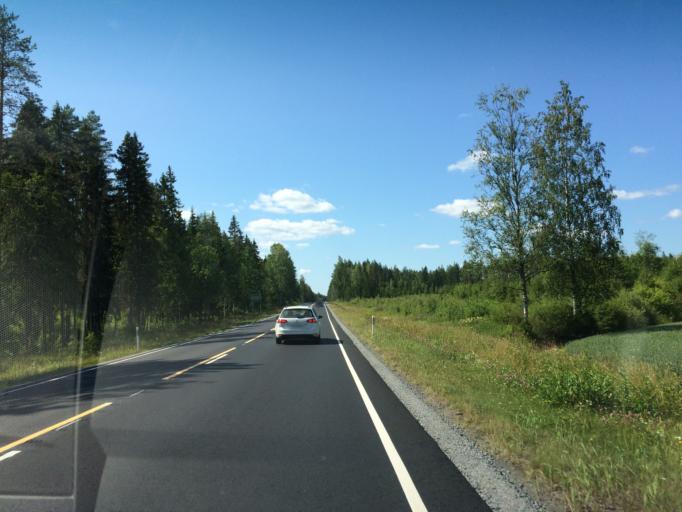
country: FI
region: Pirkanmaa
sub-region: Lounais-Pirkanmaa
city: Kiikoinen
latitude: 61.4742
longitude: 22.5413
